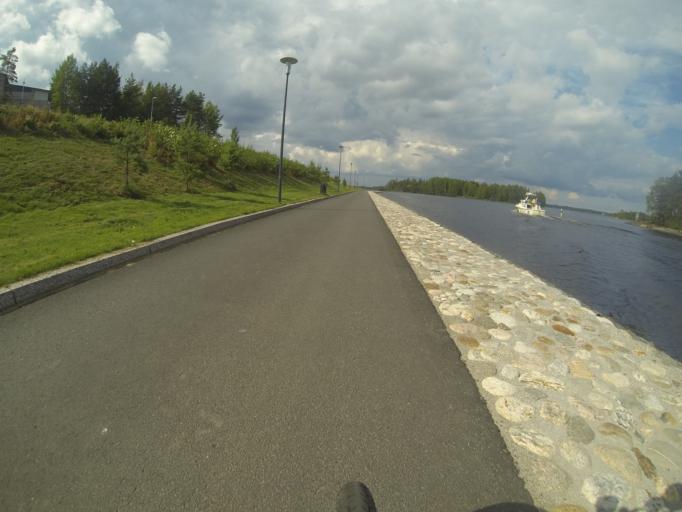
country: FI
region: Southern Savonia
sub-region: Savonlinna
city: Savonlinna
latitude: 61.8722
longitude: 28.8821
